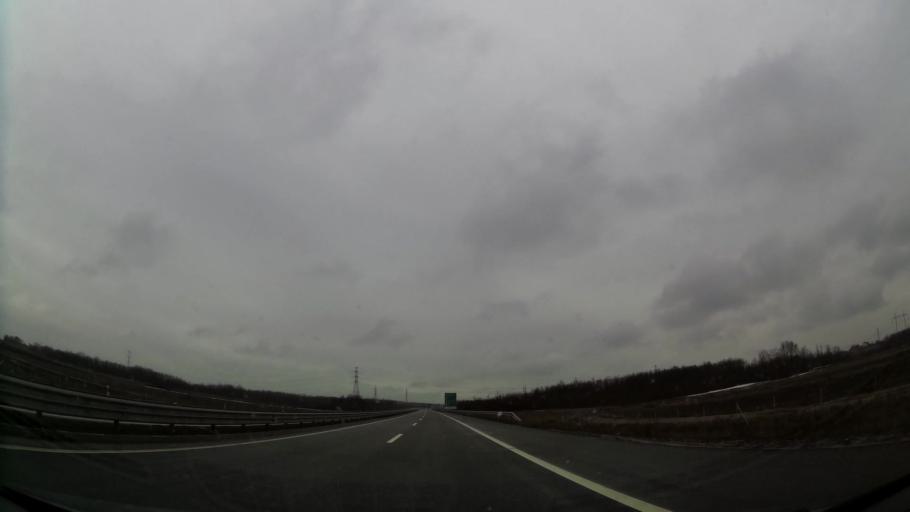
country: XK
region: Ferizaj
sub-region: Komuna e Ferizajt
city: Ferizaj
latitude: 42.3806
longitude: 21.2031
